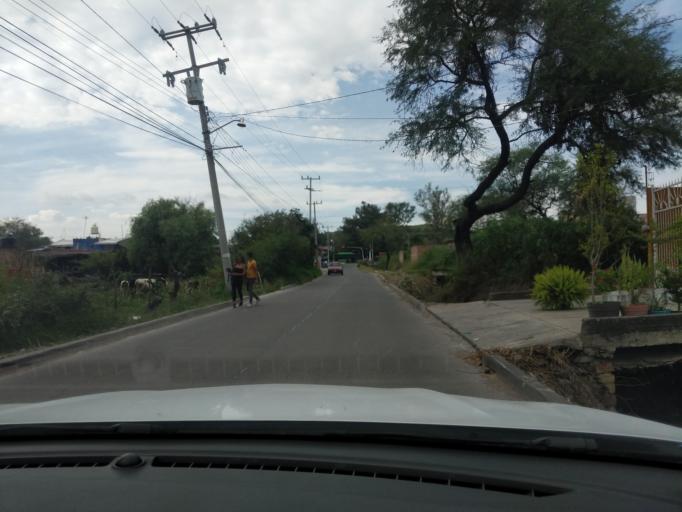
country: MX
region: Jalisco
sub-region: El Salto
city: Galaxia Bonito Jalisco
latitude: 20.5110
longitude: -103.1902
